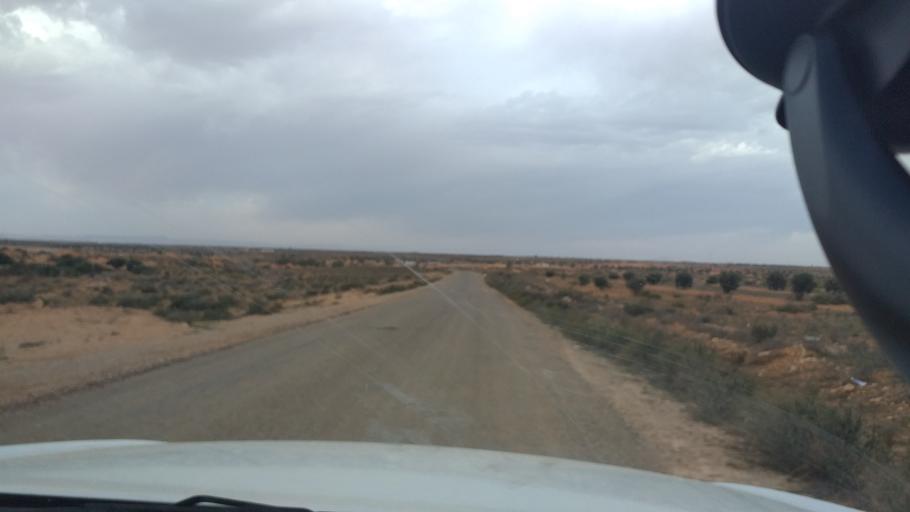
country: TN
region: Madanin
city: Medenine
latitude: 33.3173
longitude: 10.6126
